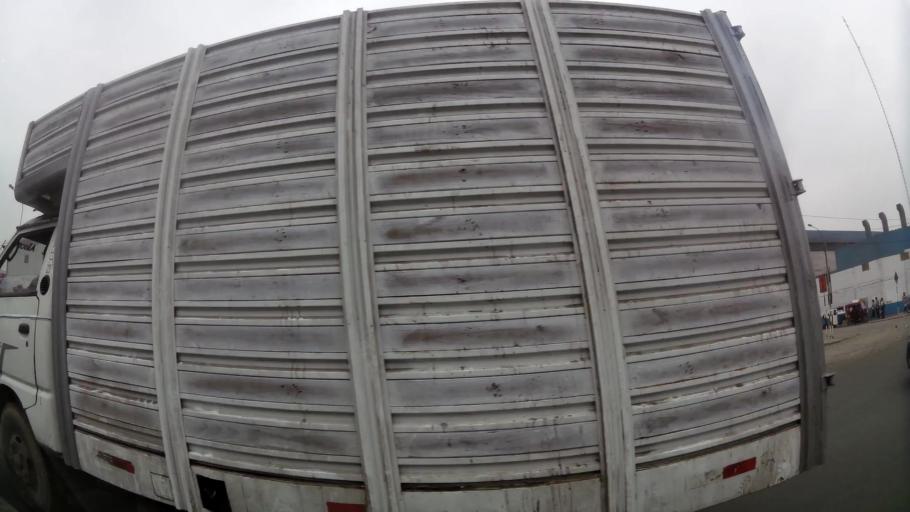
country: PE
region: Lima
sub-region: Lima
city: Vitarte
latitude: -12.0524
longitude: -76.9592
